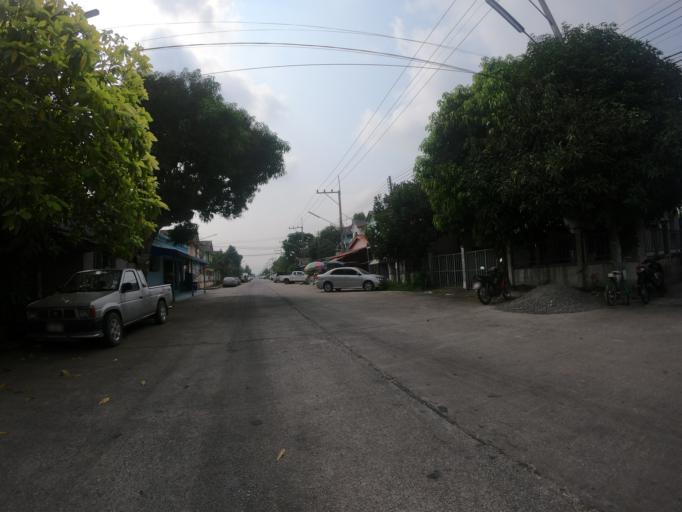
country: TH
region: Pathum Thani
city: Nong Suea
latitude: 14.0752
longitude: 100.8585
